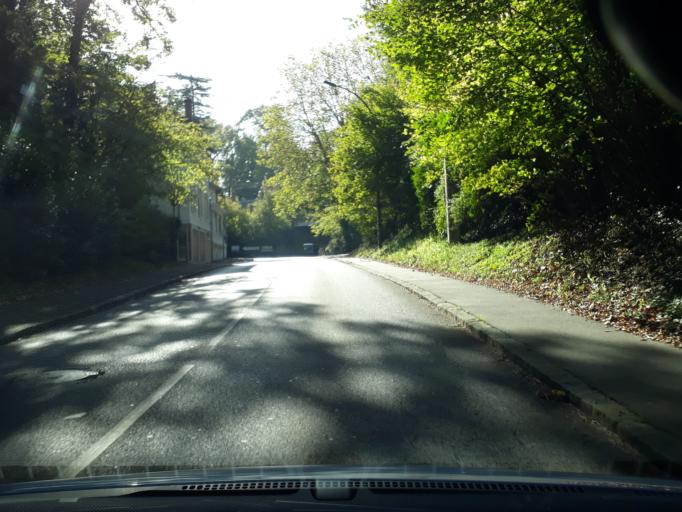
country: FR
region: Ile-de-France
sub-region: Departement de Seine-et-Marne
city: Bois-le-Roi
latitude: 48.4756
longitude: 2.6934
